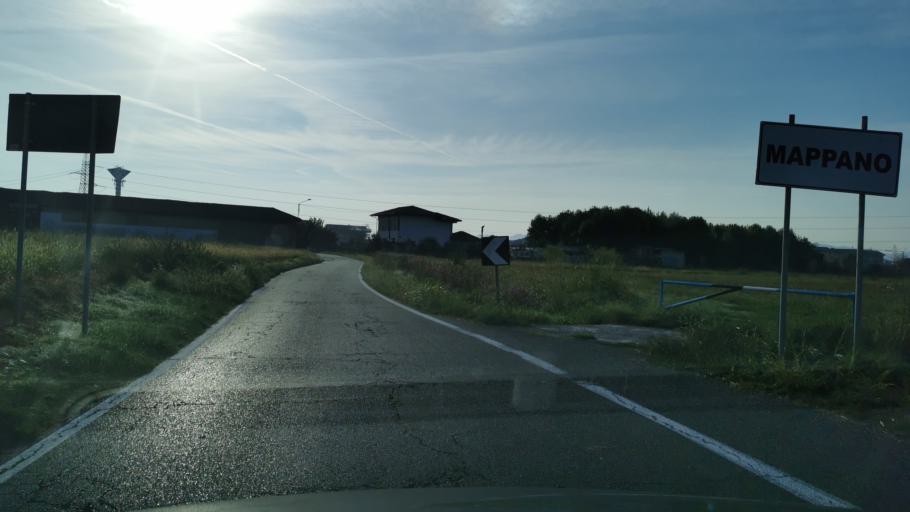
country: IT
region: Piedmont
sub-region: Provincia di Torino
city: Leini
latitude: 45.1569
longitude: 7.6928
